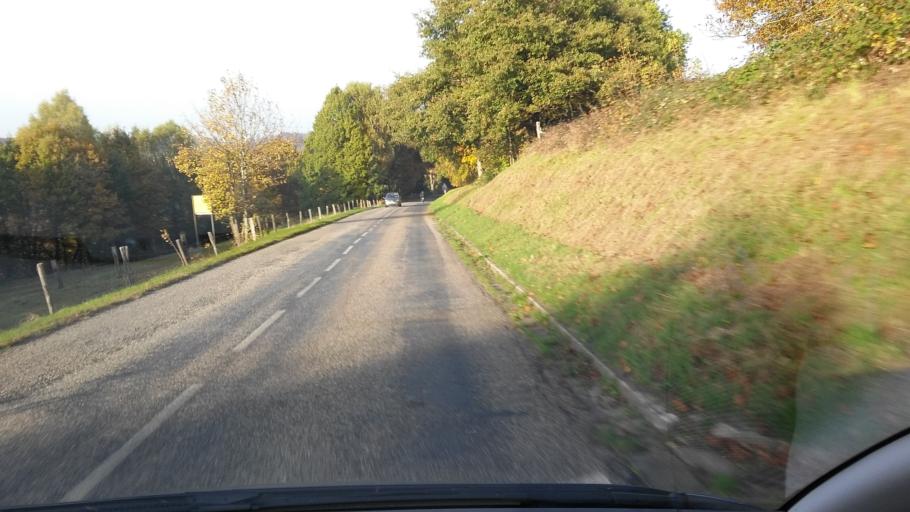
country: FR
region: Lorraine
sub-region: Departement de la Moselle
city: Dabo
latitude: 48.6877
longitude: 7.2055
